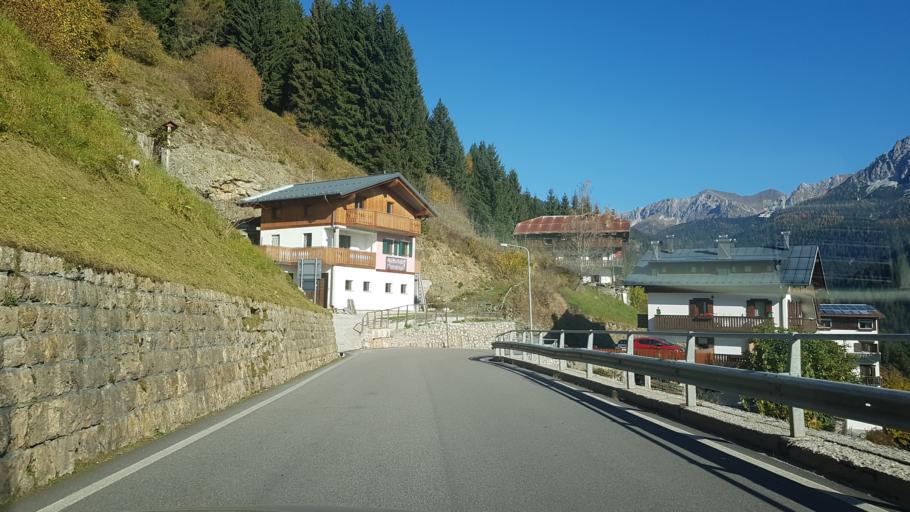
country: IT
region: Veneto
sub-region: Provincia di Belluno
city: Candide
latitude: 46.5921
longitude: 12.5193
